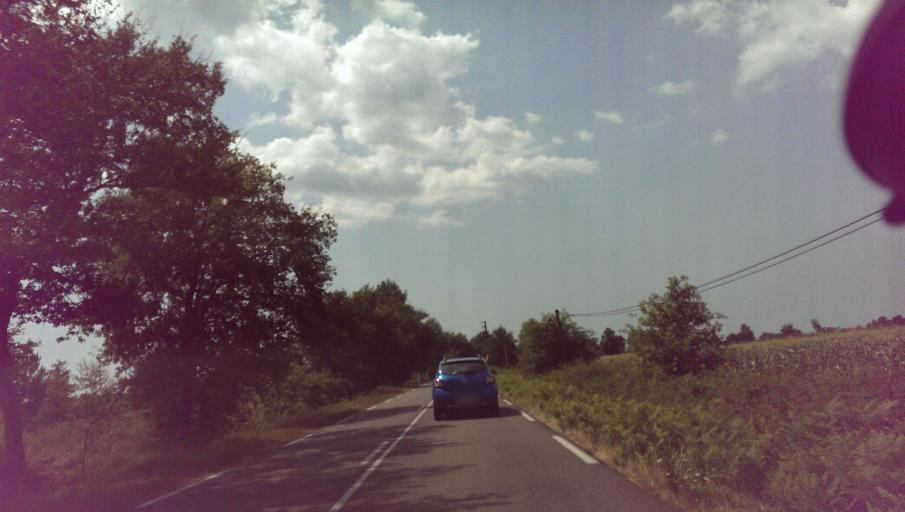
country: FR
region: Aquitaine
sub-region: Departement des Landes
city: Sabres
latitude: 44.1251
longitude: -0.6835
